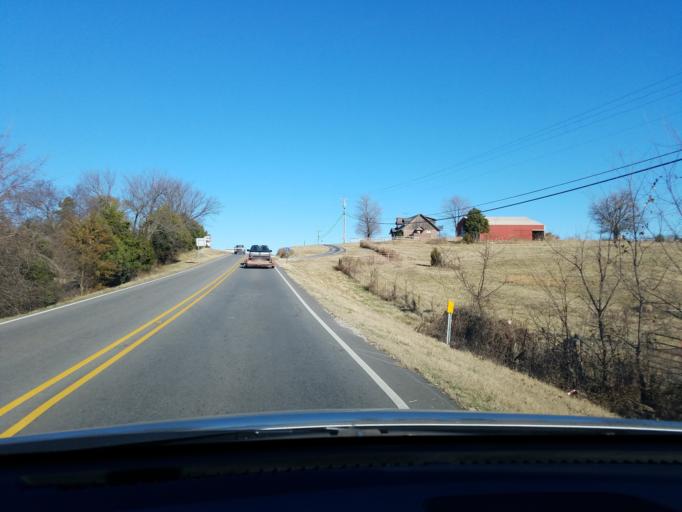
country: US
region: Arkansas
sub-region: Carroll County
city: Berryville
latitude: 36.3897
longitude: -93.5662
